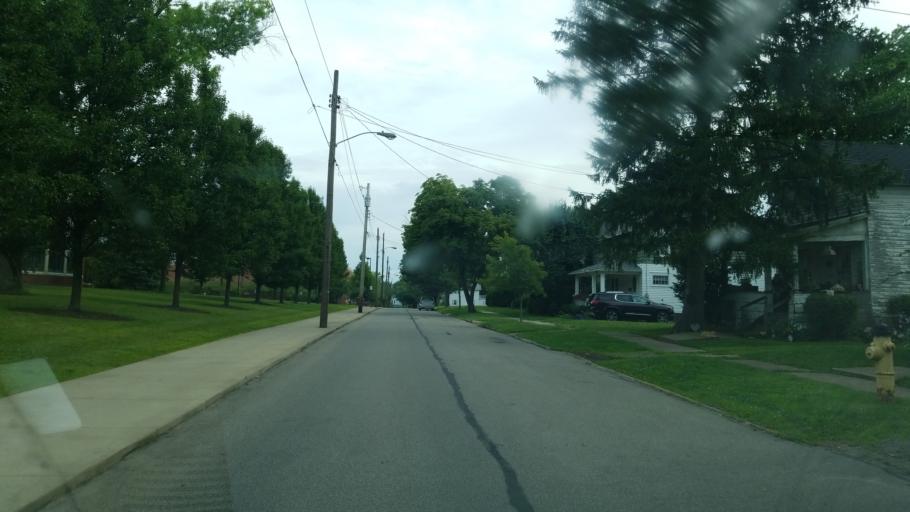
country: US
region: Ohio
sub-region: Ashland County
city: Ashland
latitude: 40.8596
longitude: -82.3181
